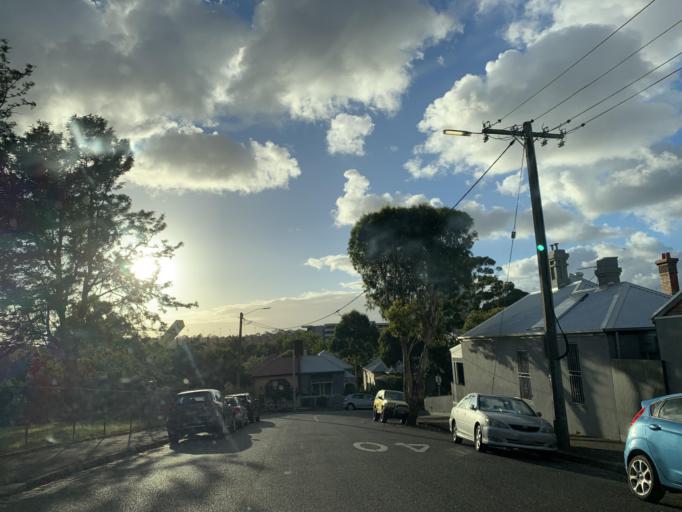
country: AU
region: Victoria
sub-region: Moonee Valley
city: Travancore
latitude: -37.7823
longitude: 144.9356
